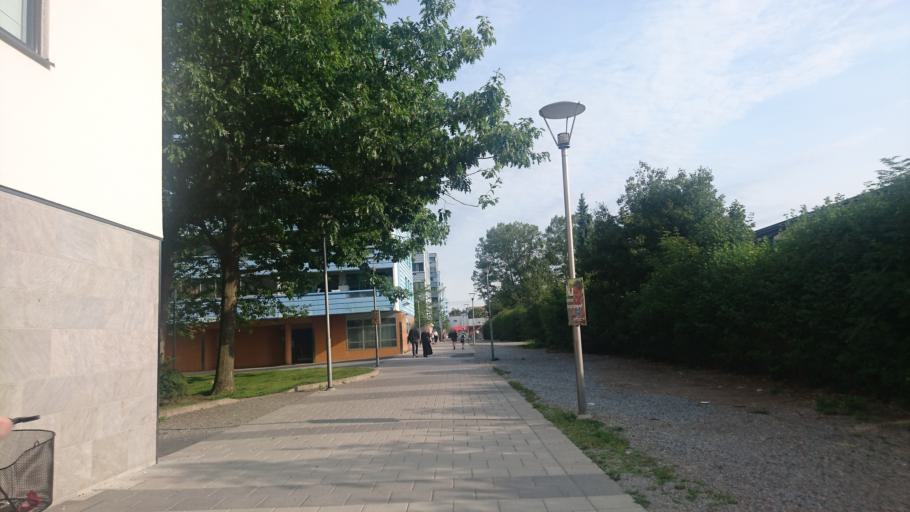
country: SE
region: Stockholm
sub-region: Upplands Vasby Kommun
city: Upplands Vaesby
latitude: 59.5153
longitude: 17.9116
